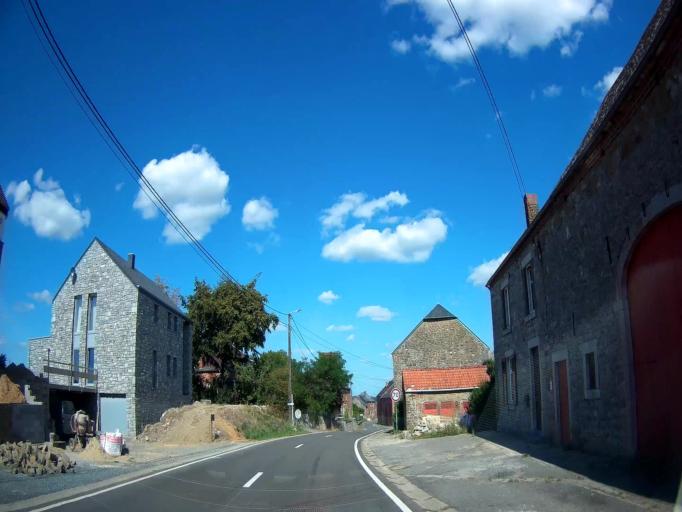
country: BE
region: Wallonia
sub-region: Province de Namur
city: Houyet
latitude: 50.2013
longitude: 4.9450
